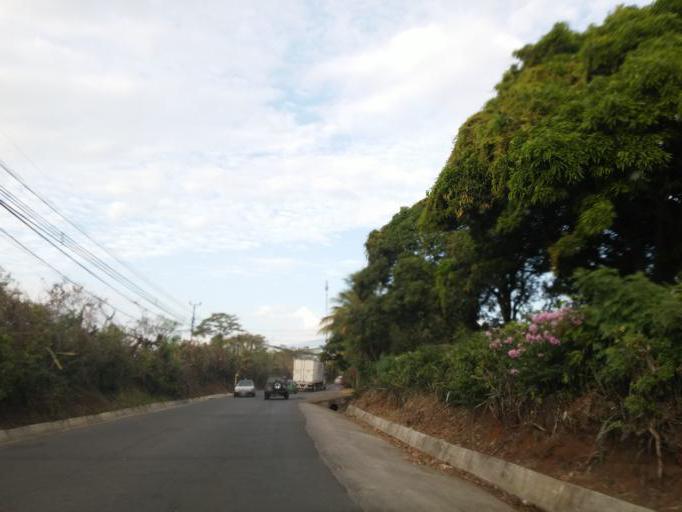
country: CR
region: Alajuela
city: Alajuela
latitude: 9.9818
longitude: -84.2247
